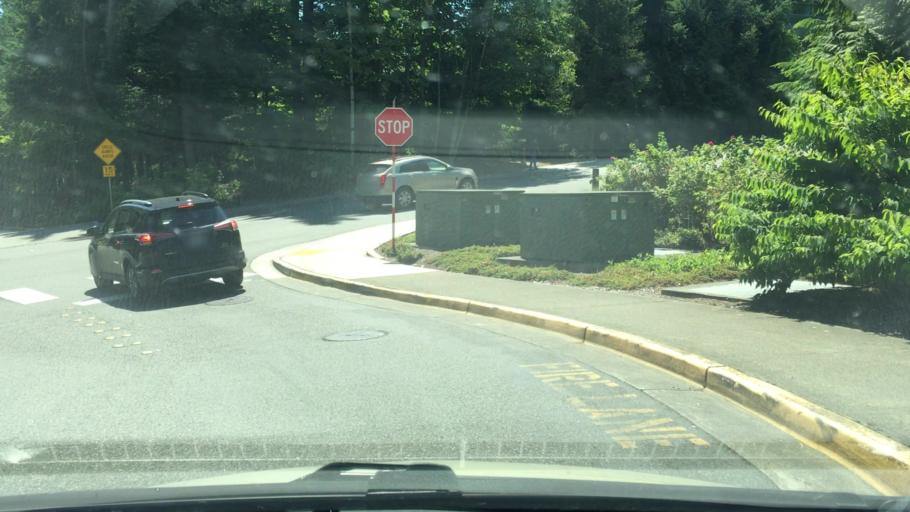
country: US
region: Washington
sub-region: King County
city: Redmond
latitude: 47.6429
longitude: -122.1239
